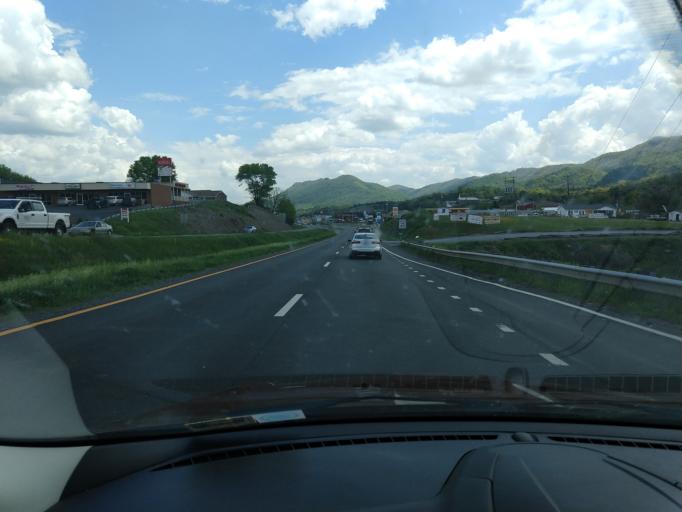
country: US
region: Virginia
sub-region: Tazewell County
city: Claypool Hill
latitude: 37.0637
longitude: -81.7451
